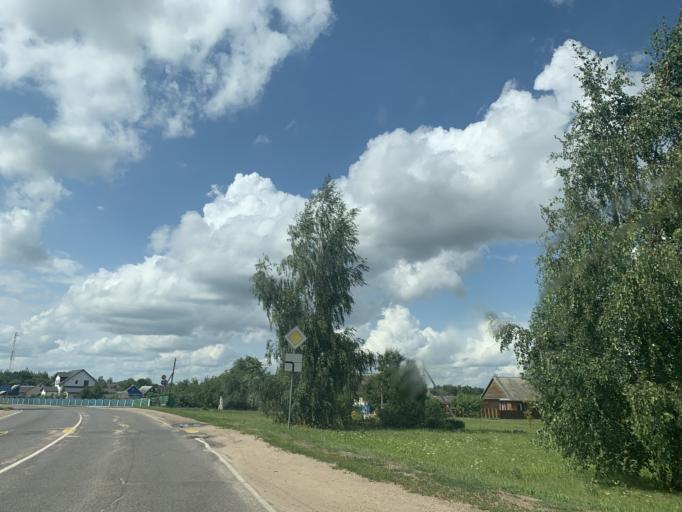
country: BY
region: Minsk
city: Enyerhyetykaw
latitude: 53.5875
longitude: 27.0525
